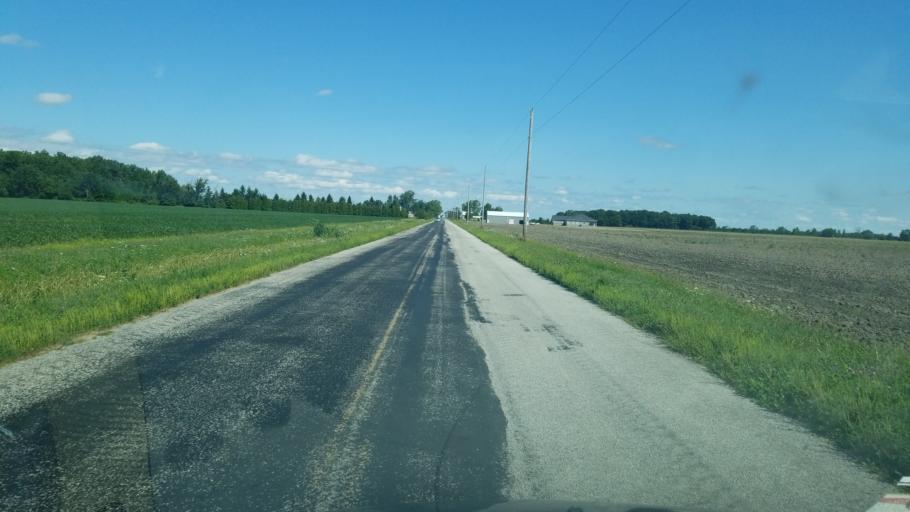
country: US
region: Ohio
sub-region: Henry County
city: Deshler
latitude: 41.2413
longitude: -83.8423
